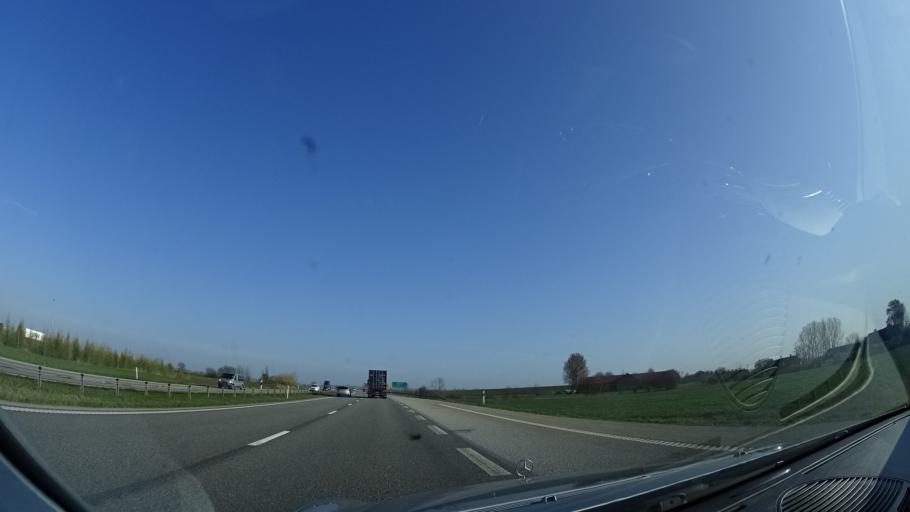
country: SE
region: Skane
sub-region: Landskrona
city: Landskrona
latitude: 55.8808
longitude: 12.8781
